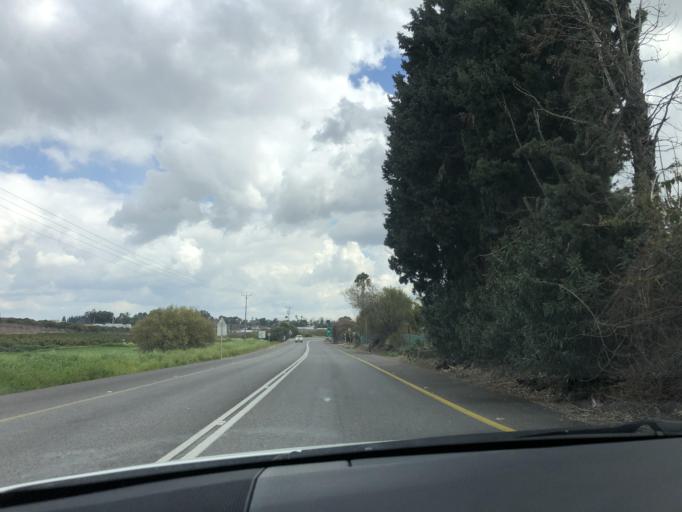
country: IL
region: Central District
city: Tel Mond
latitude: 32.2619
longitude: 34.9198
